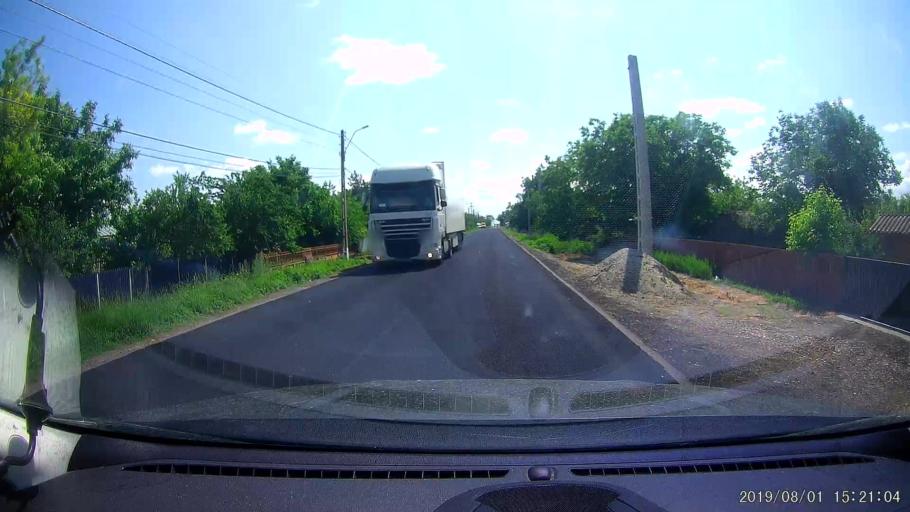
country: RO
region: Braila
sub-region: Comuna Tufesti
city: Tufesti
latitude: 45.0739
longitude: 27.8009
